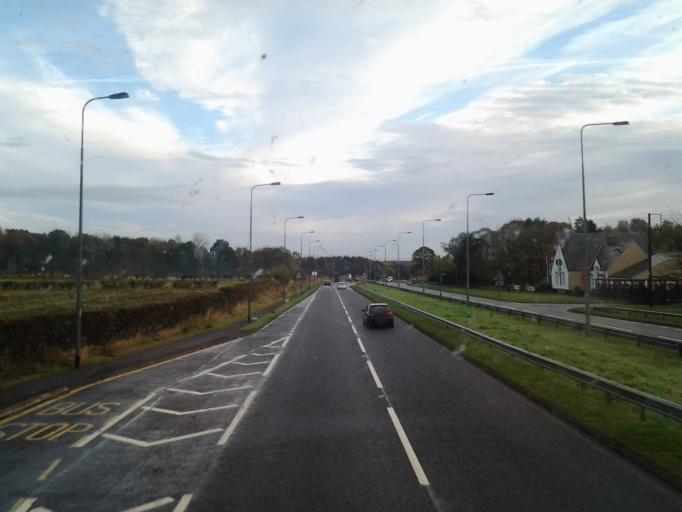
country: GB
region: England
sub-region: County Durham
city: Chester-le-Street
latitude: 54.8373
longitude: -1.5873
